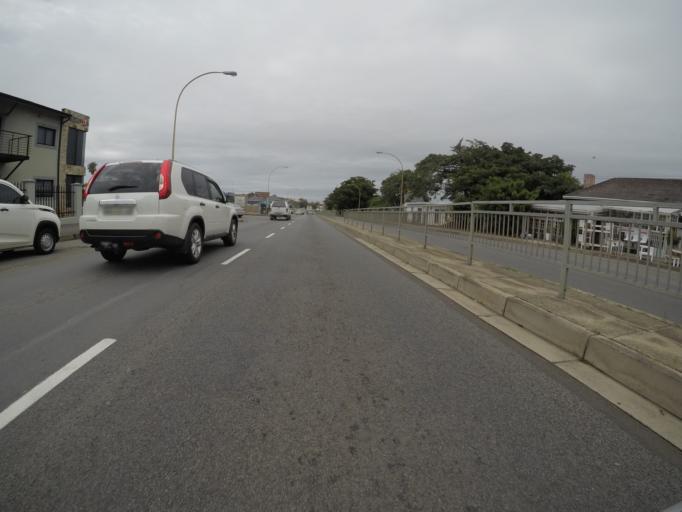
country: ZA
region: Eastern Cape
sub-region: Buffalo City Metropolitan Municipality
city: East London
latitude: -32.9775
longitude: 27.8994
